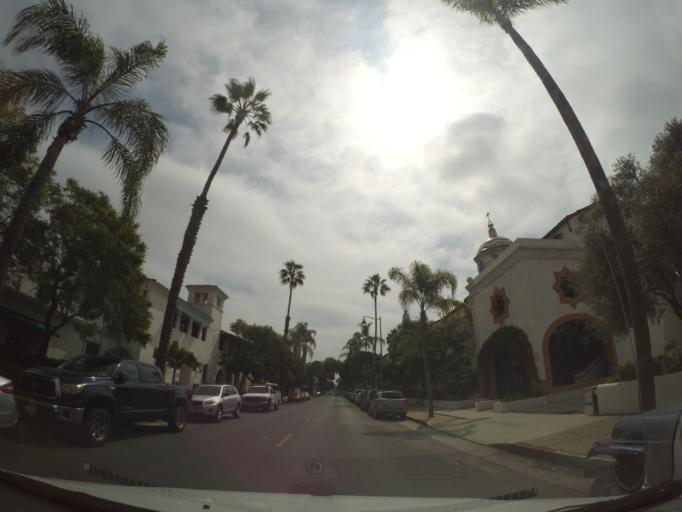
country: US
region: California
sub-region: Santa Barbara County
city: Santa Barbara
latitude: 34.4217
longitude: -119.6944
